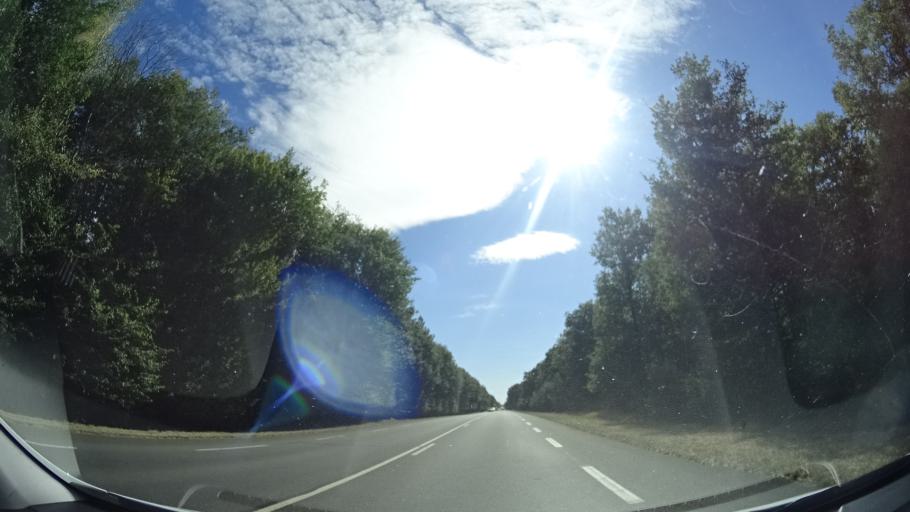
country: FR
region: Centre
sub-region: Departement du Loiret
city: Vitry-aux-Loges
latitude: 47.9278
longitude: 2.3338
